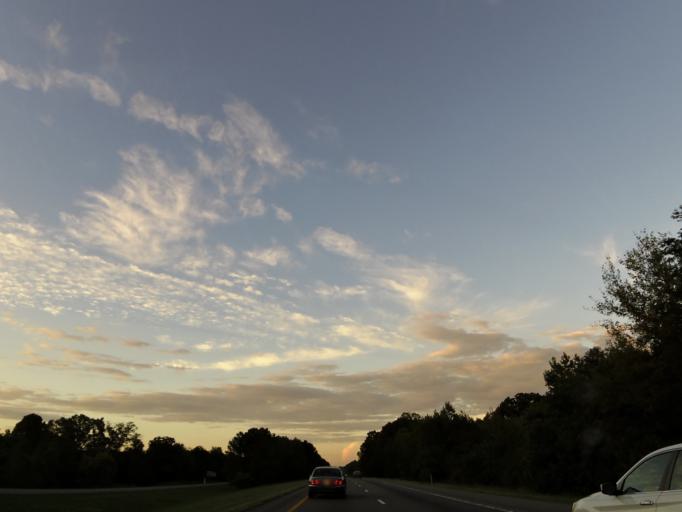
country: US
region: Tennessee
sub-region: McMinn County
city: Athens
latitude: 35.5223
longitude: -84.5921
